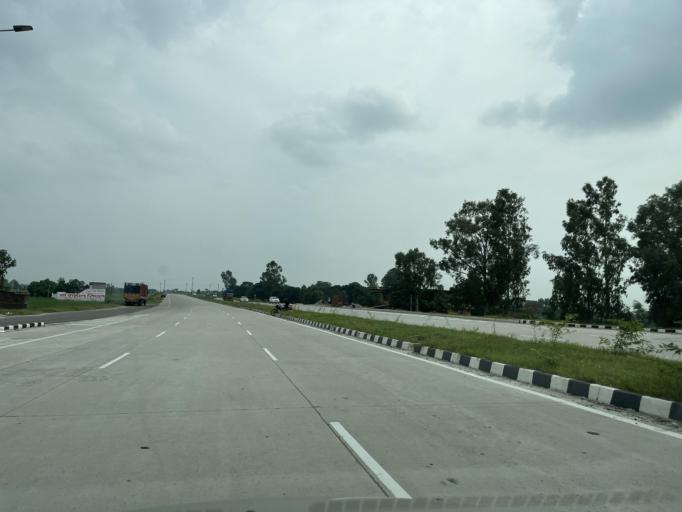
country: IN
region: Uttarakhand
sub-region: Udham Singh Nagar
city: Kashipur
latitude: 29.2056
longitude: 78.9309
